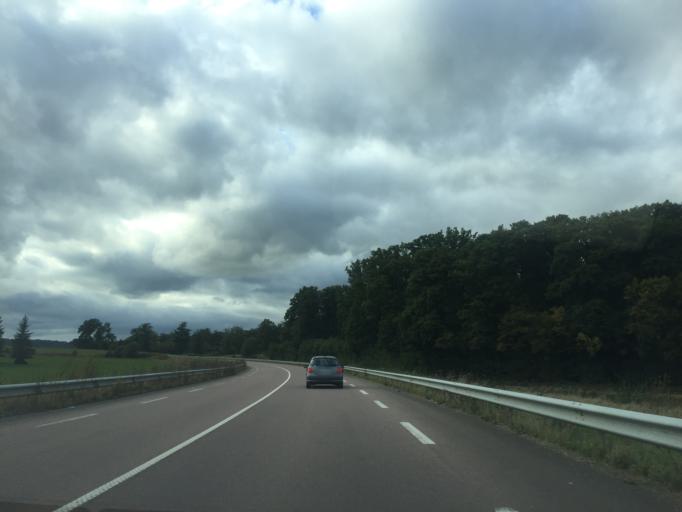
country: FR
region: Lorraine
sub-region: Departement des Vosges
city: Chatenois
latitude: 48.2987
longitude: 5.8808
